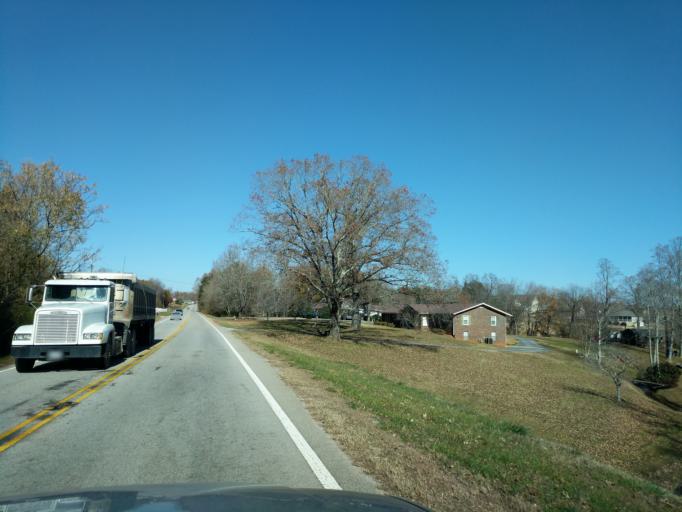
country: US
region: South Carolina
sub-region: Spartanburg County
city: Landrum
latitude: 35.1064
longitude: -82.2254
